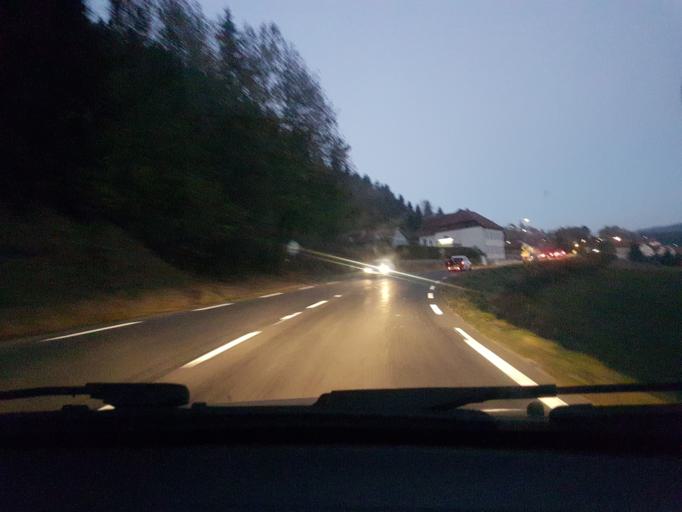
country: FR
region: Franche-Comte
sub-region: Departement du Doubs
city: Les Fins
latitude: 47.0773
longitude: 6.6187
